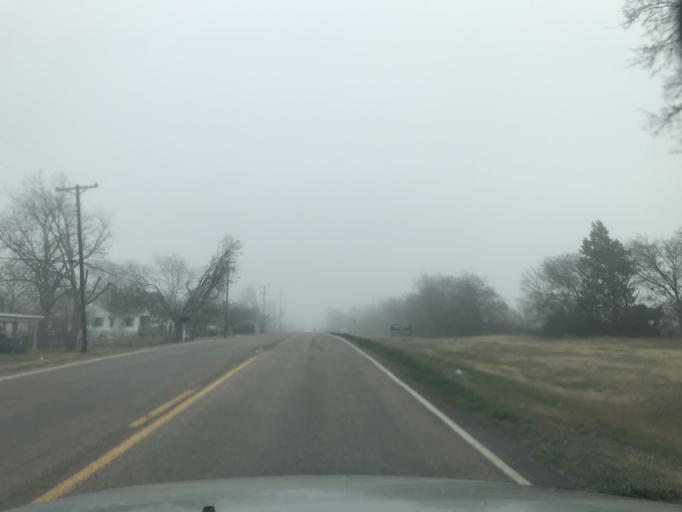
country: US
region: Texas
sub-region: Hunt County
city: Caddo Mills
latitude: 33.0679
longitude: -96.2242
